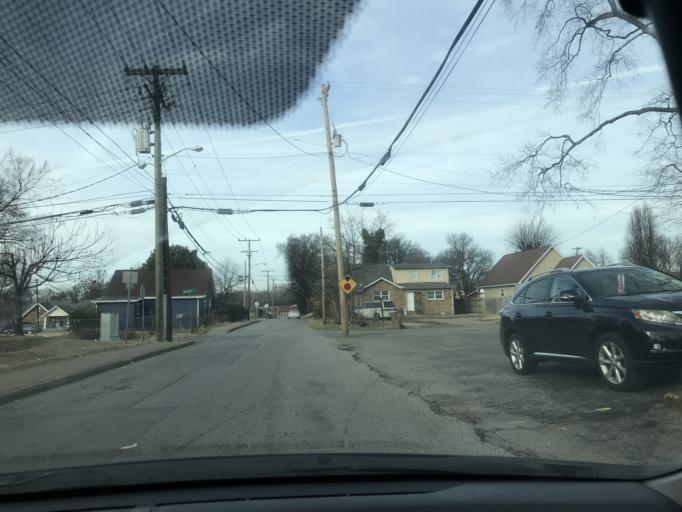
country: US
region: Tennessee
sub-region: Davidson County
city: Nashville
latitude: 36.1684
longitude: -86.8169
